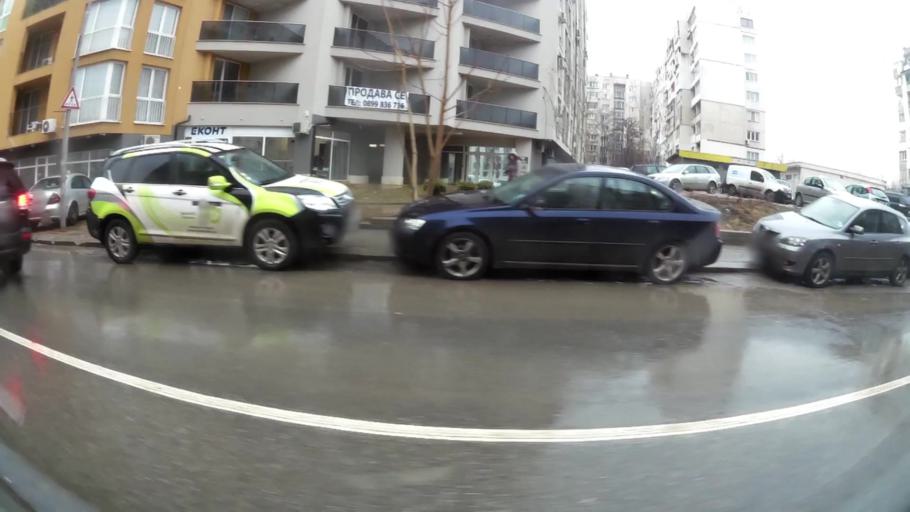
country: BG
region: Sofia-Capital
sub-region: Stolichna Obshtina
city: Sofia
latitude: 42.6265
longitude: 23.3837
